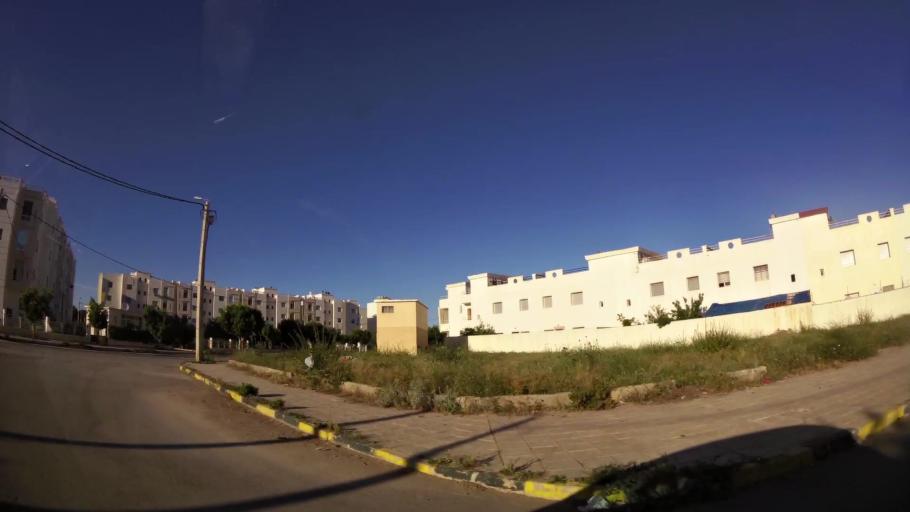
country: MA
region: Oriental
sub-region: Berkane-Taourirt
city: Madagh
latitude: 35.0860
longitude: -2.2488
